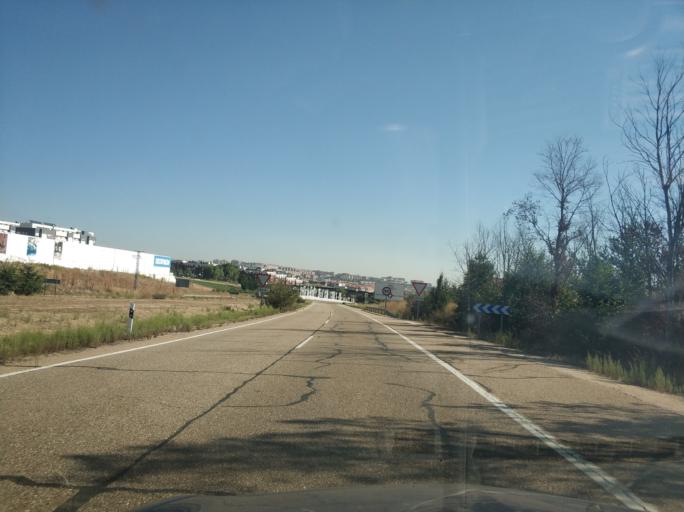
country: ES
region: Castille and Leon
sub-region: Provincia de Valladolid
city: Arroyo
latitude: 41.6161
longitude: -4.7884
